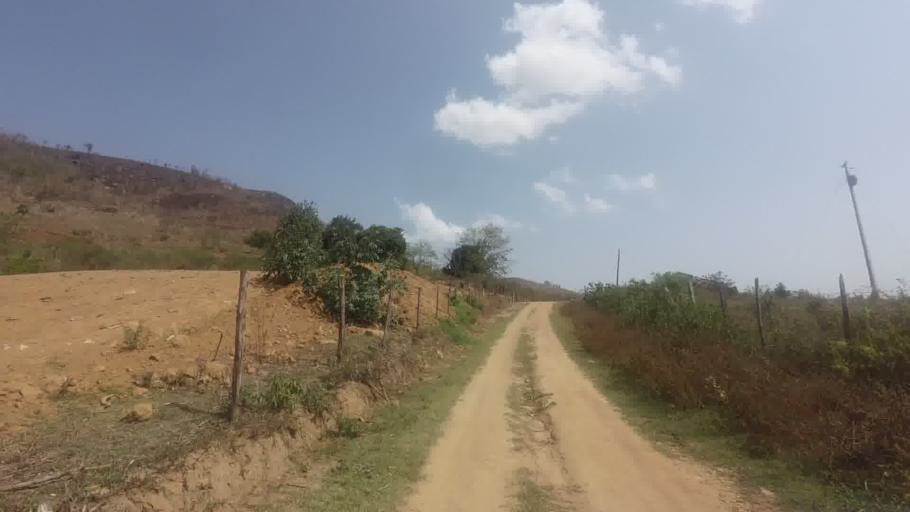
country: BR
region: Espirito Santo
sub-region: Sao Jose Do Calcado
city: Sao Jose do Calcado
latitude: -21.0296
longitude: -41.5171
